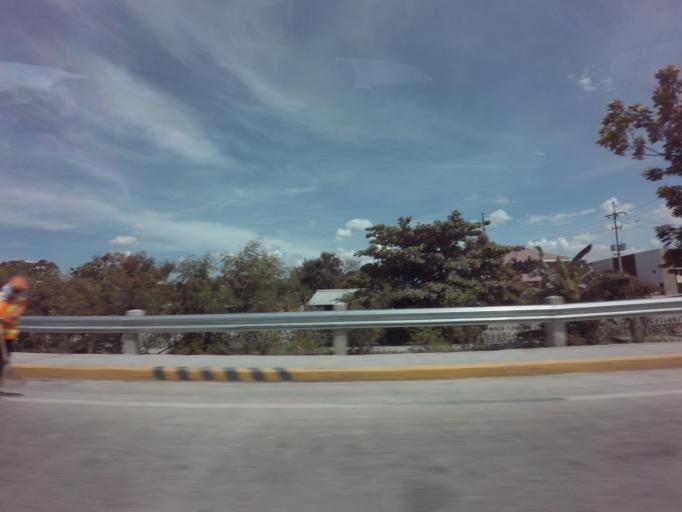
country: PH
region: Calabarzon
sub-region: Province of Rizal
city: Taguig
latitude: 14.5151
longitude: 121.0743
